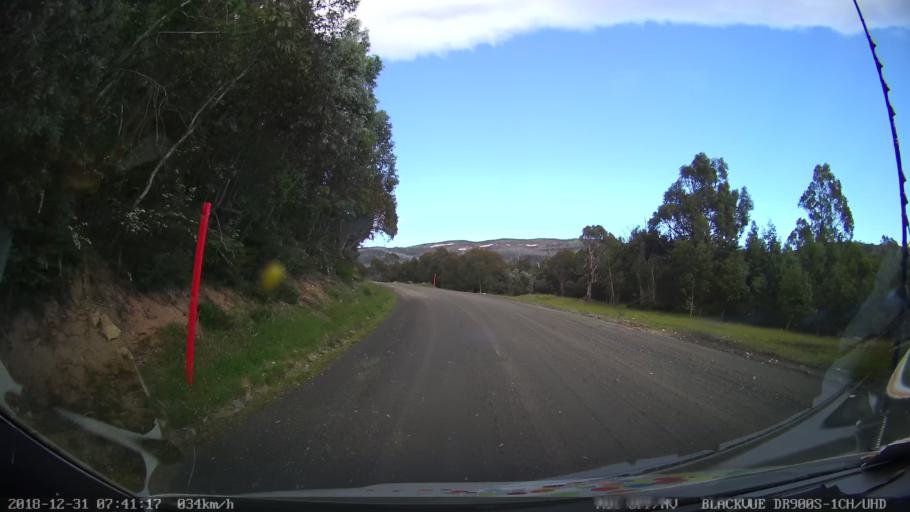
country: AU
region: New South Wales
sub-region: Snowy River
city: Jindabyne
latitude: -36.3528
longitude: 148.4128
